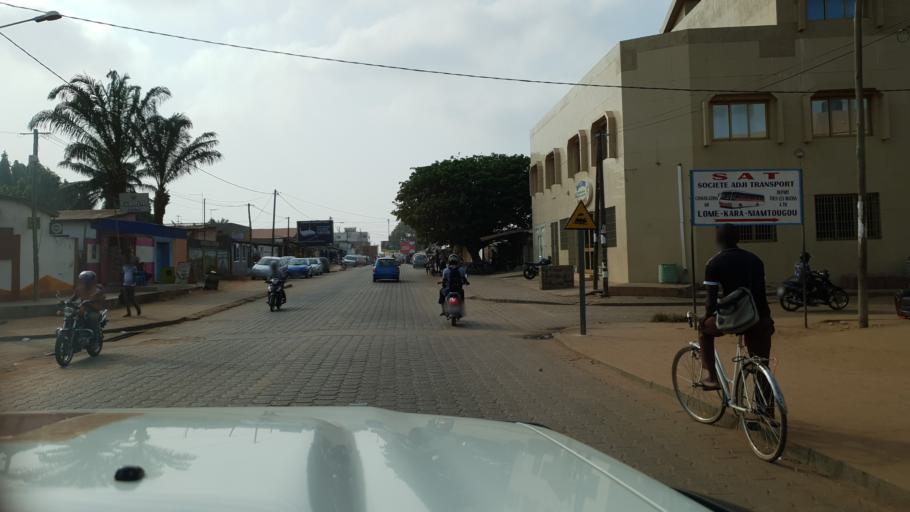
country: TG
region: Maritime
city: Lome
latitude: 6.1582
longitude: 1.2159
